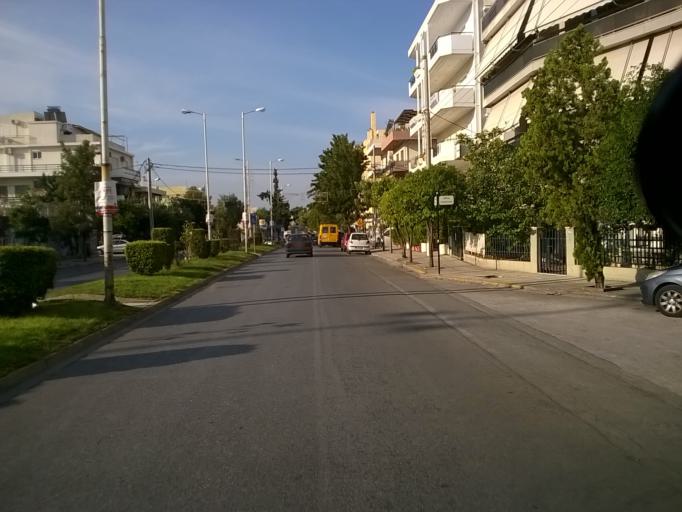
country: GR
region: Attica
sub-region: Nomarchia Athinas
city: Alimos
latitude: 37.9186
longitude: 23.7352
